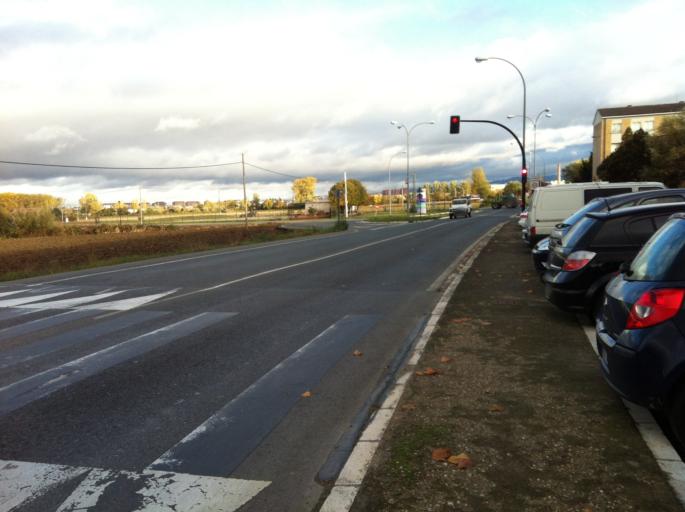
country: ES
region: Basque Country
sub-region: Provincia de Alava
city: Gasteiz / Vitoria
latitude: 42.8618
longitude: -2.7307
